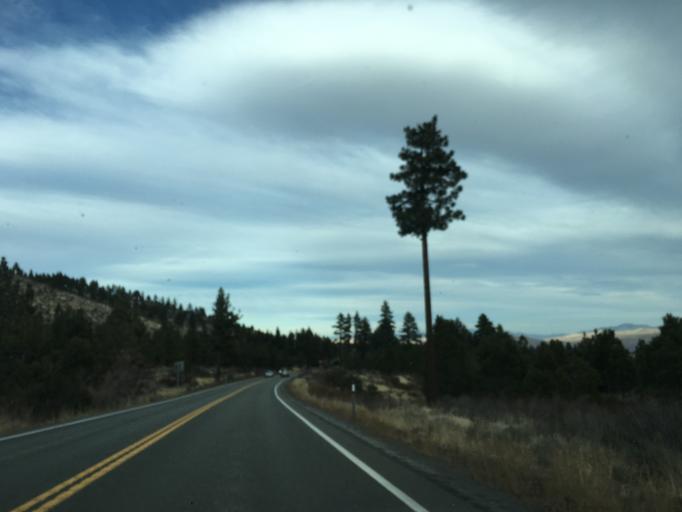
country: US
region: Nevada
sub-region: Washoe County
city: Reno
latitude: 39.3687
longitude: -119.8473
